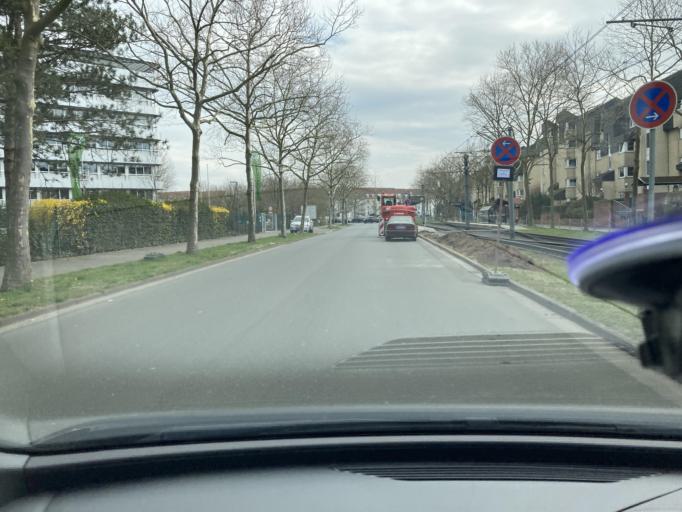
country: DE
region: Hesse
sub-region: Regierungsbezirk Darmstadt
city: Darmstadt
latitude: 49.9036
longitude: 8.6800
